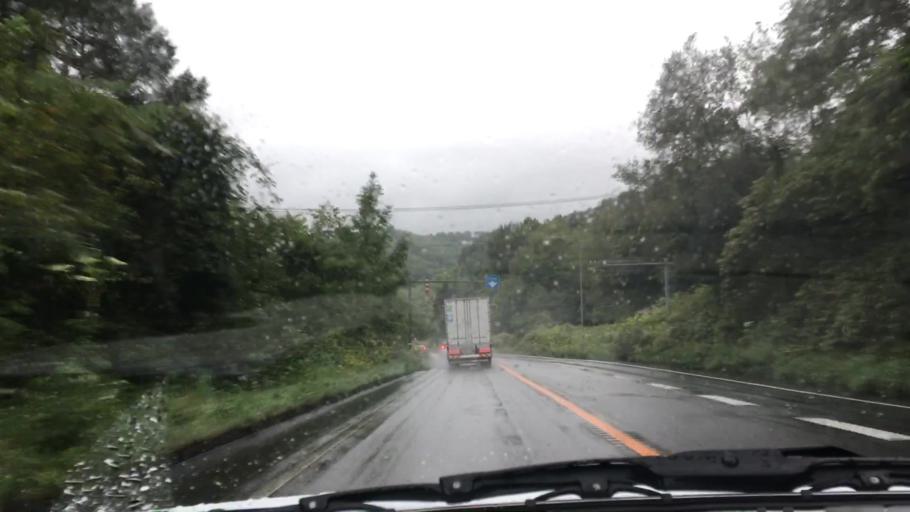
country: JP
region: Hokkaido
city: Niseko Town
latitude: 42.5997
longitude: 140.6638
